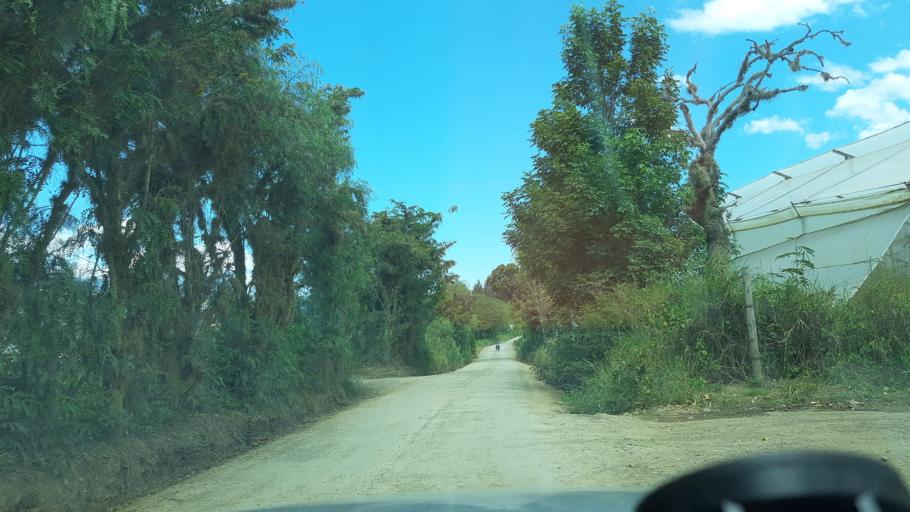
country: CO
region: Boyaca
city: Villa de Leiva
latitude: 5.6586
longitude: -73.5727
